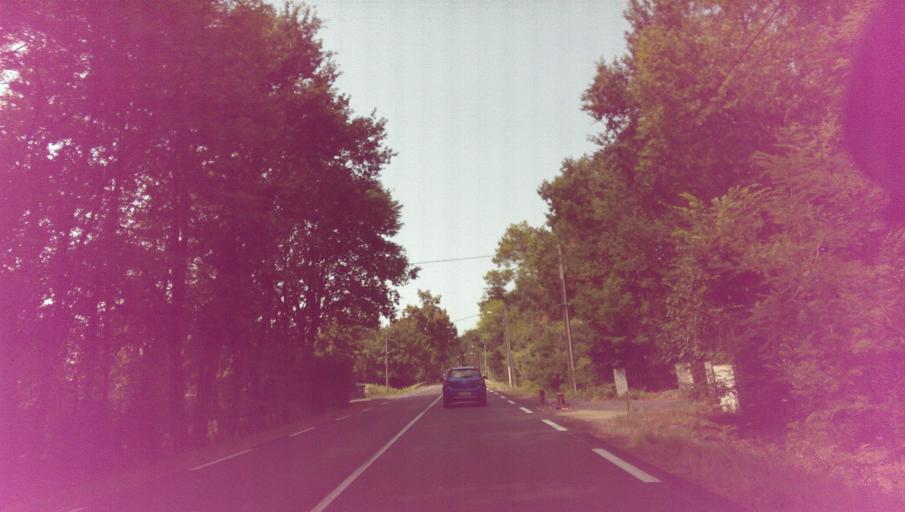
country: FR
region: Aquitaine
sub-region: Departement des Landes
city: Sabres
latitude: 44.1433
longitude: -0.7292
